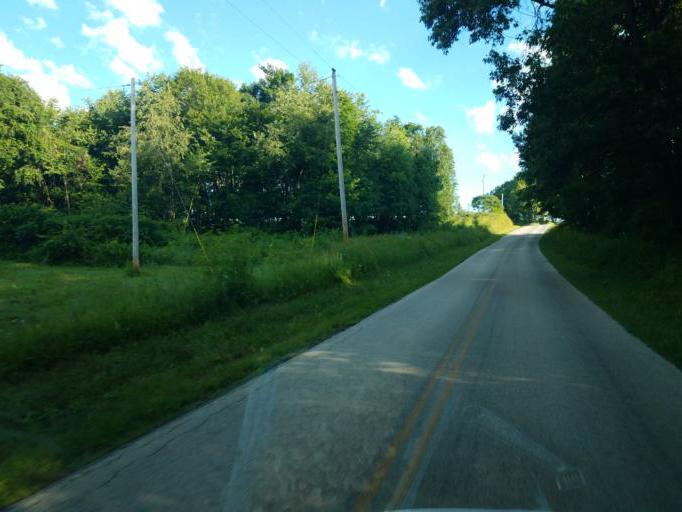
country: US
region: Ohio
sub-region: Ashland County
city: Loudonville
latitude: 40.5815
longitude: -82.3631
